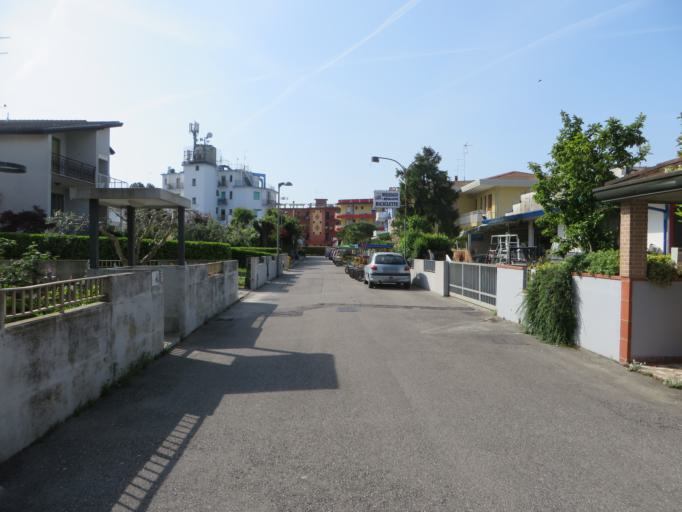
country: IT
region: Veneto
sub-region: Provincia di Venezia
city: Crepaldo
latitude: 45.5477
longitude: 12.7577
